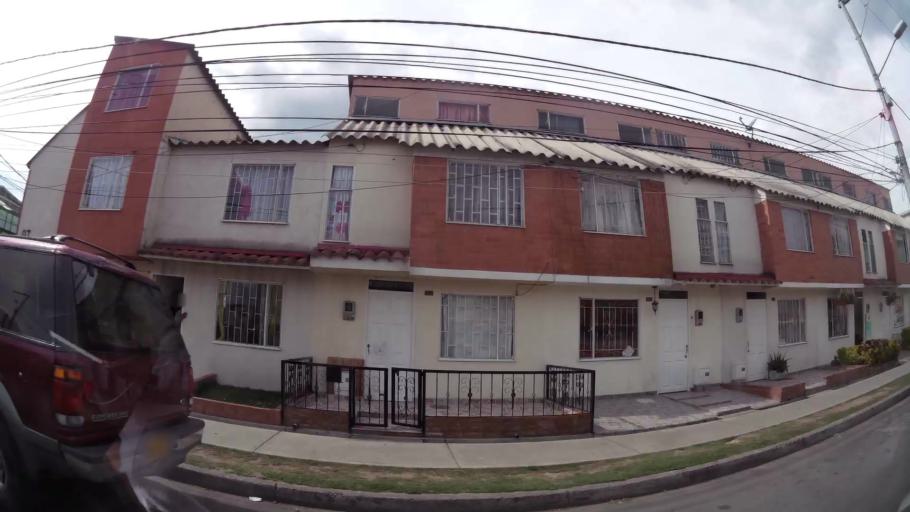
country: CO
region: Cundinamarca
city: Funza
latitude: 4.7104
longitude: -74.2012
